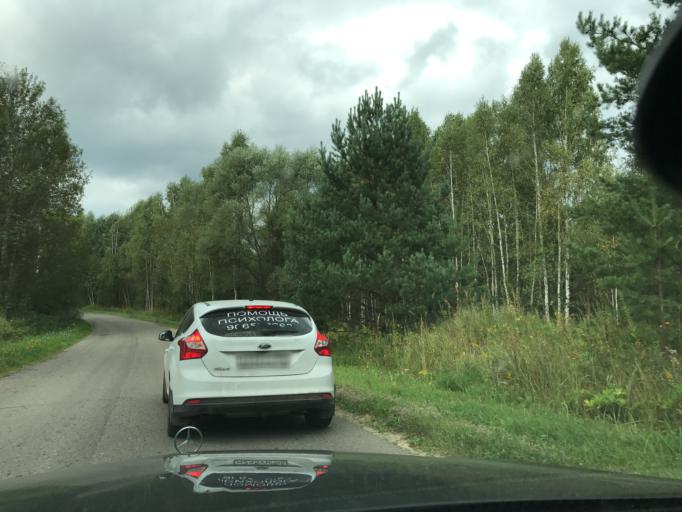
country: RU
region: Vladimir
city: Galitsy
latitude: 55.9969
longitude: 42.8454
